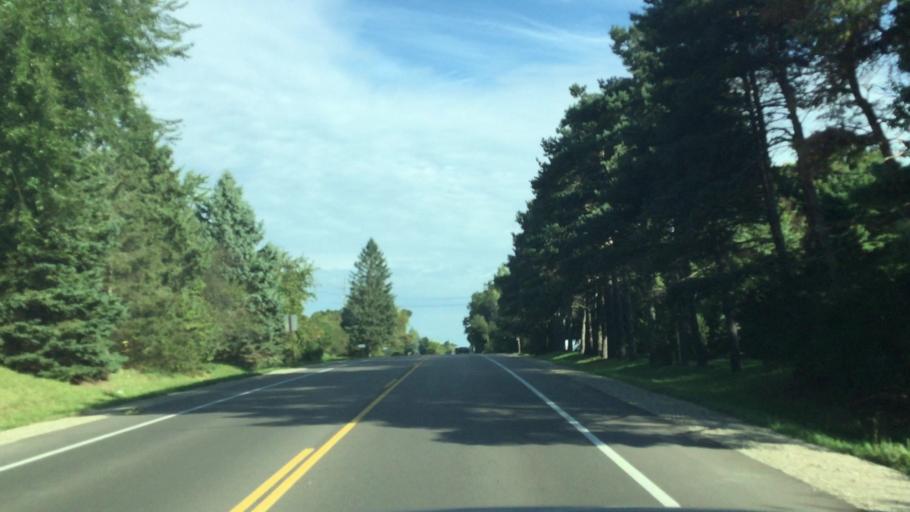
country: US
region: Michigan
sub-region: Livingston County
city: Howell
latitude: 42.6044
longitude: -83.8746
